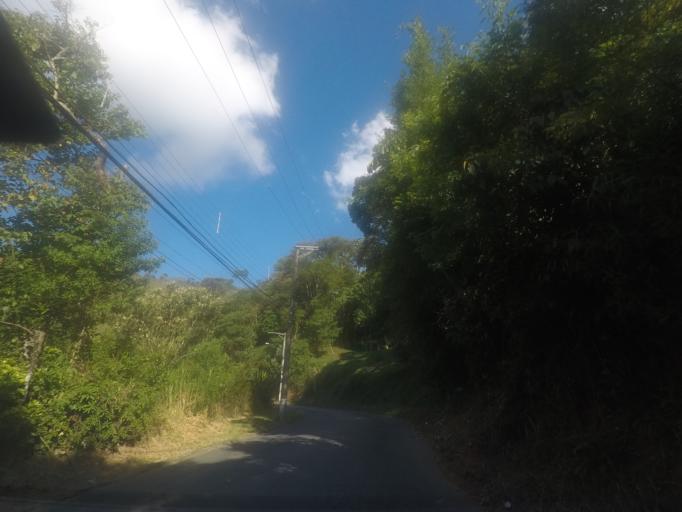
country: BR
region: Rio de Janeiro
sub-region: Petropolis
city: Petropolis
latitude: -22.5060
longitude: -43.1562
